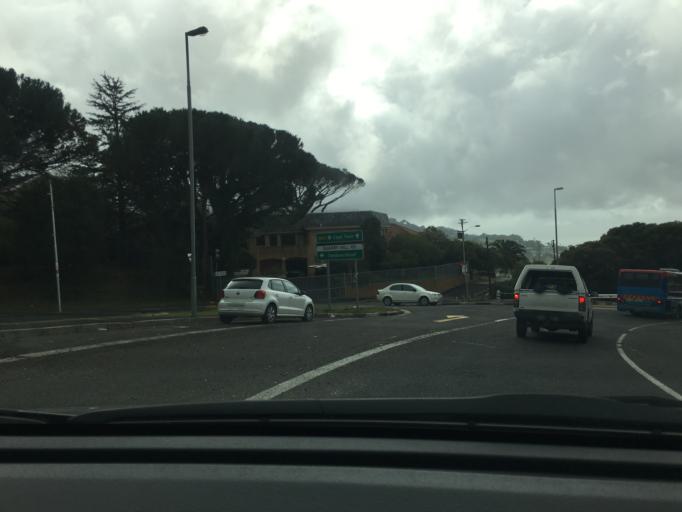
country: ZA
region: Western Cape
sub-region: City of Cape Town
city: Cape Town
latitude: -33.9347
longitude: 18.4022
